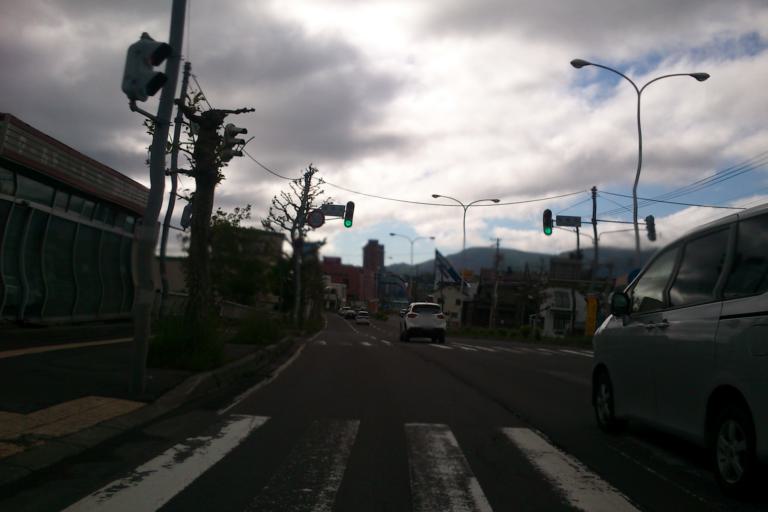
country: JP
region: Hokkaido
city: Otaru
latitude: 43.1871
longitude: 141.0118
